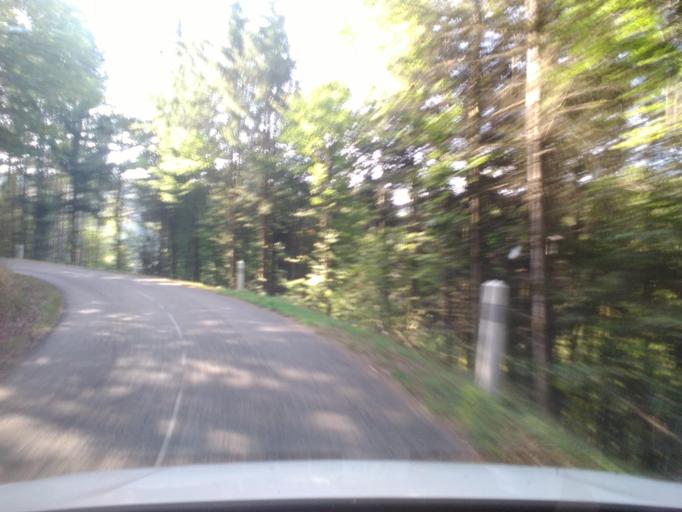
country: FR
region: Lorraine
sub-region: Departement des Vosges
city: Senones
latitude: 48.3835
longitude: 7.0378
